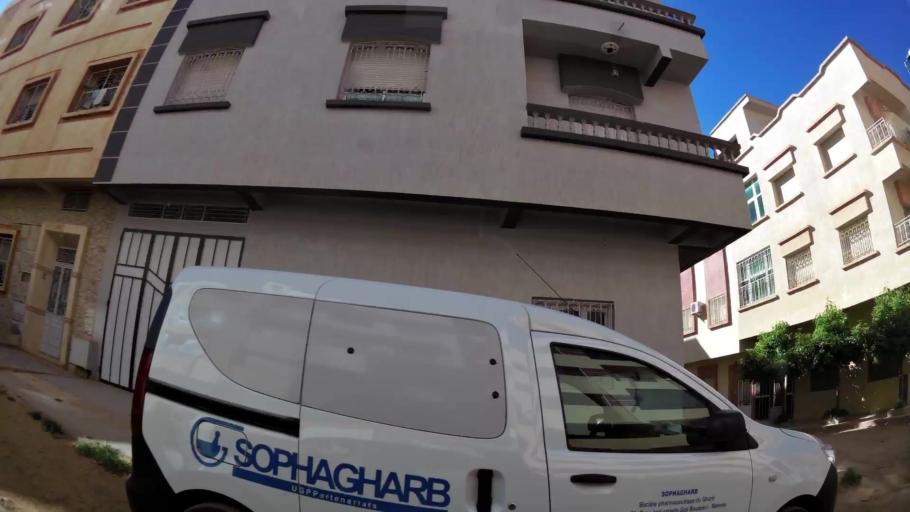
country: MA
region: Meknes-Tafilalet
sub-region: Meknes
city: Meknes
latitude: 33.8723
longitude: -5.5840
